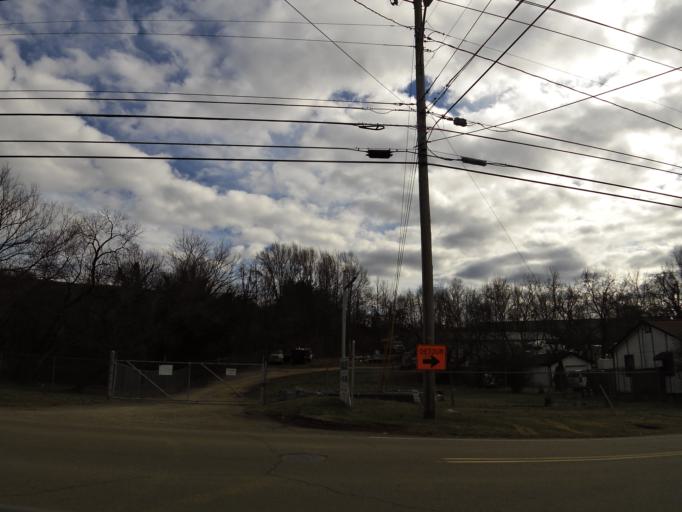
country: US
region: Tennessee
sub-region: Knox County
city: Knoxville
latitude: 35.9902
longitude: -83.9077
